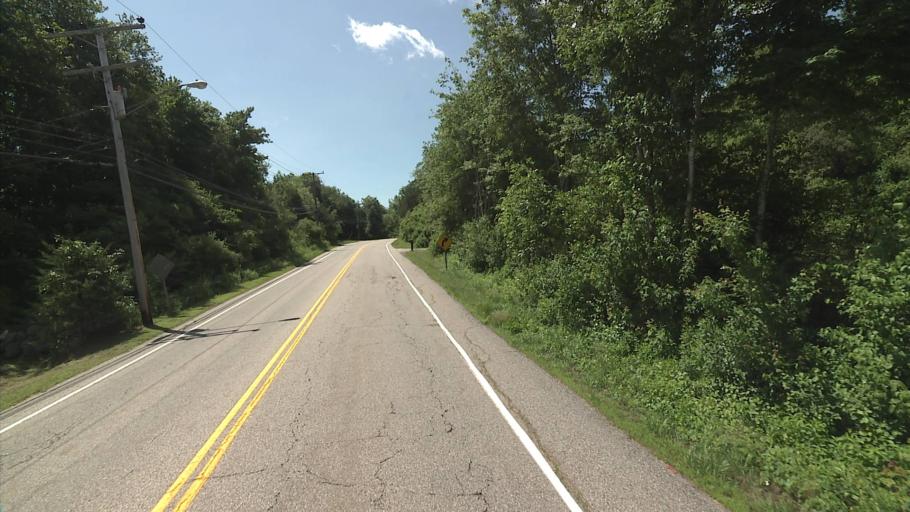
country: US
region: Connecticut
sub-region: New London County
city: Pawcatuck
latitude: 41.3481
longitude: -71.8932
